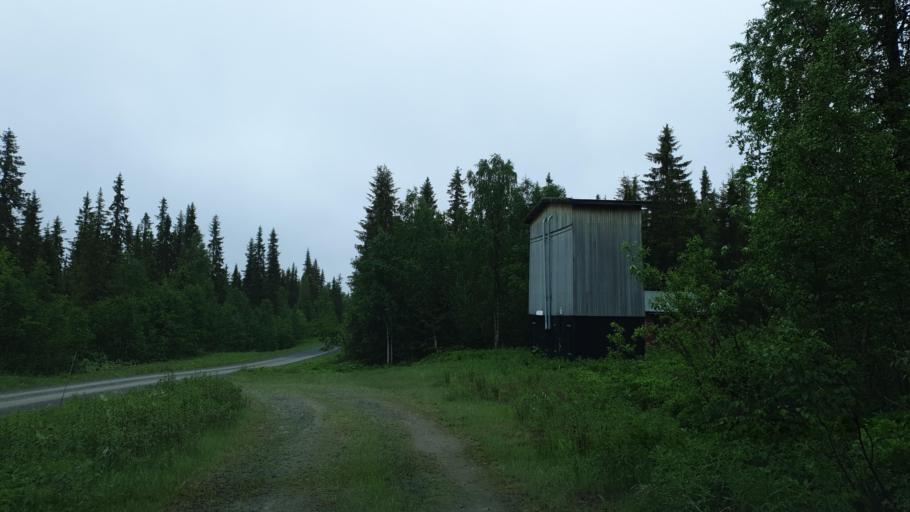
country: SE
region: Vaesterbotten
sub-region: Vilhelmina Kommun
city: Sjoberg
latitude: 65.2772
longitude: 15.8961
